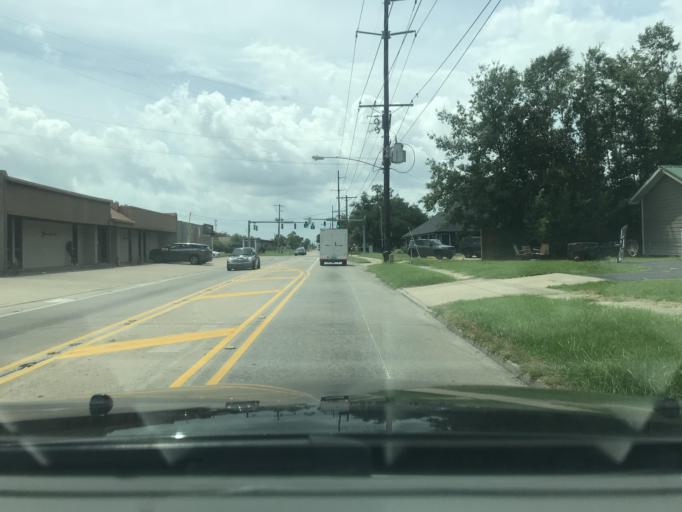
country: US
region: Louisiana
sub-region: Calcasieu Parish
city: Lake Charles
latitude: 30.2132
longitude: -93.2032
